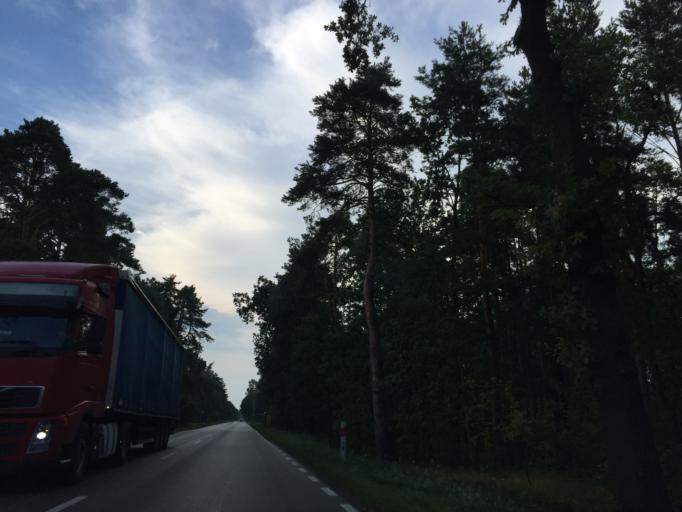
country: PL
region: Masovian Voivodeship
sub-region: Powiat ostrowski
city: Brok
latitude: 52.6757
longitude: 21.8504
